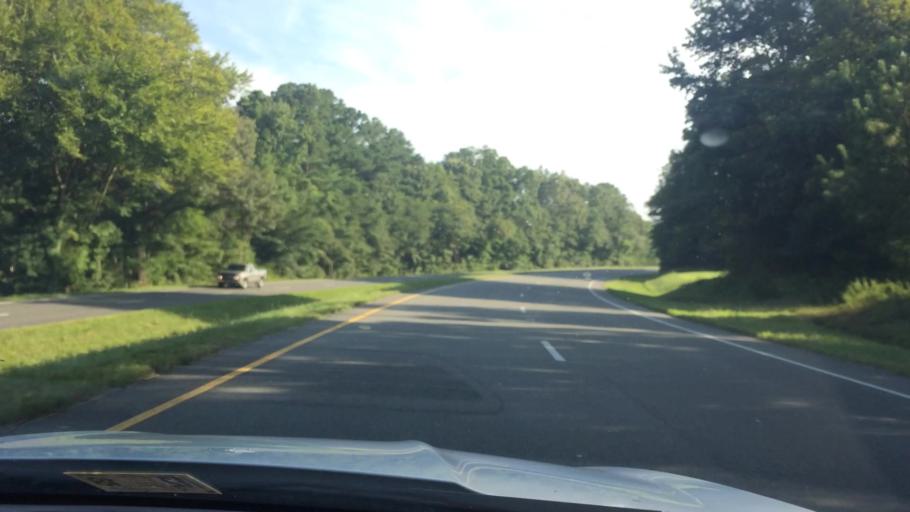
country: US
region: Virginia
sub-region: Gloucester County
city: Gloucester Courthouse
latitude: 37.4586
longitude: -76.4684
